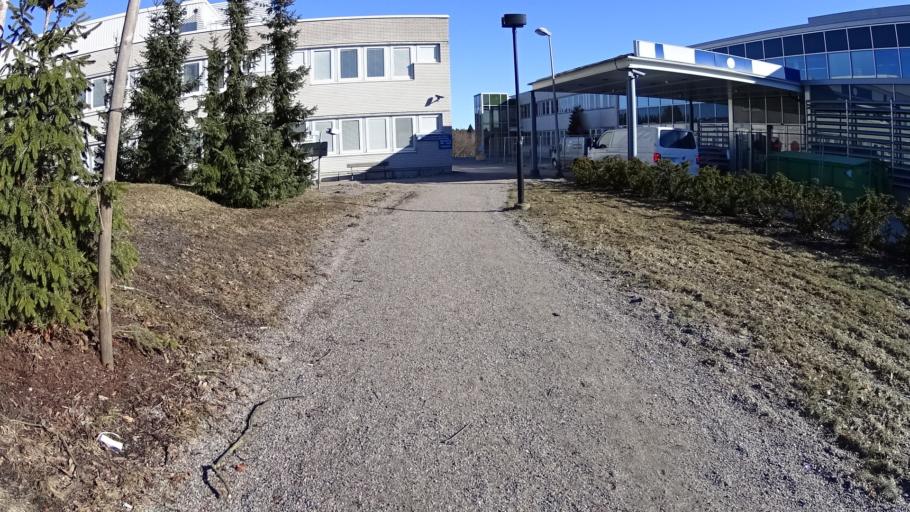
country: FI
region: Uusimaa
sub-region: Helsinki
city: Espoo
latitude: 60.2223
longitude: 24.6874
